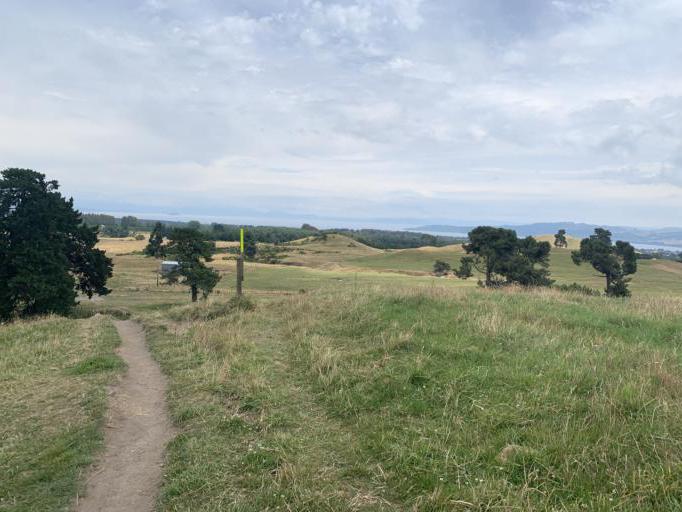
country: NZ
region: Waikato
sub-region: Taupo District
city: Taupo
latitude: -38.7029
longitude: 176.1415
